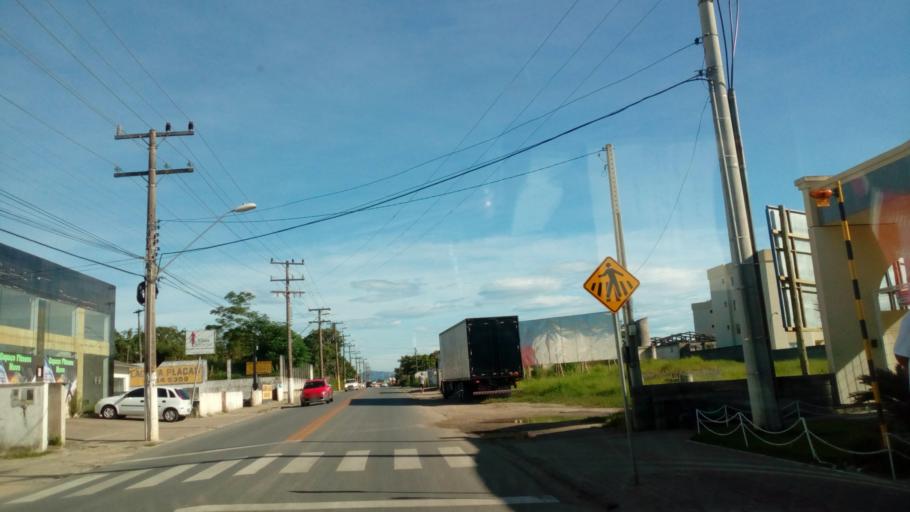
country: BR
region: Santa Catarina
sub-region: Laguna
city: Laguna
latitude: -28.4676
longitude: -48.7852
